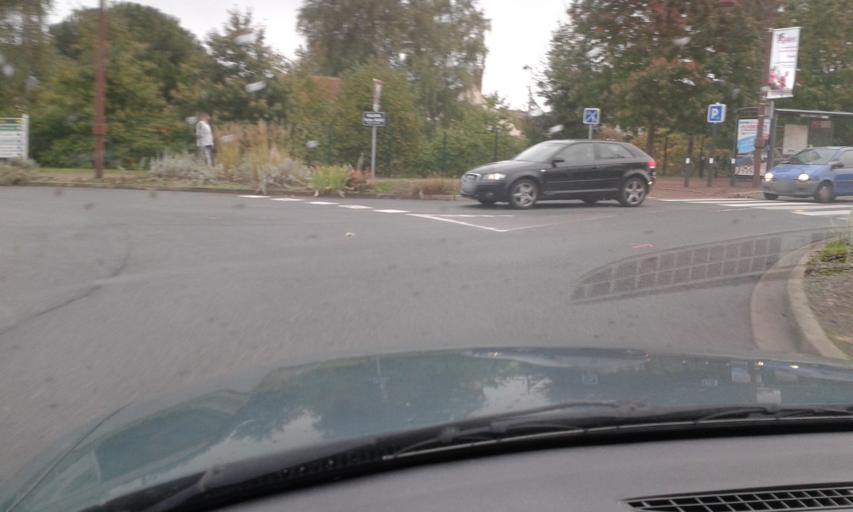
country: FR
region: Centre
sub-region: Departement du Loiret
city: Olivet
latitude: 47.8567
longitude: 1.8950
